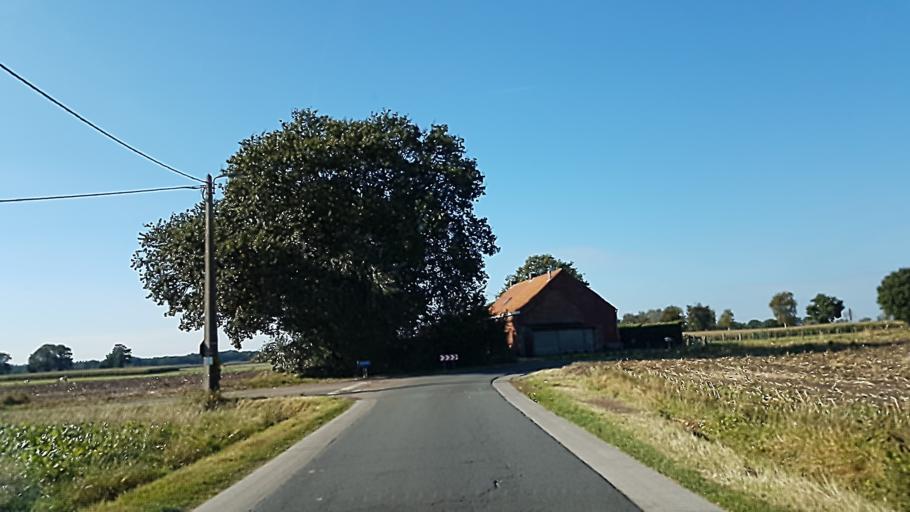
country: BE
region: Flanders
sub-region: Provincie Antwerpen
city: Essen
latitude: 51.4333
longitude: 4.4078
